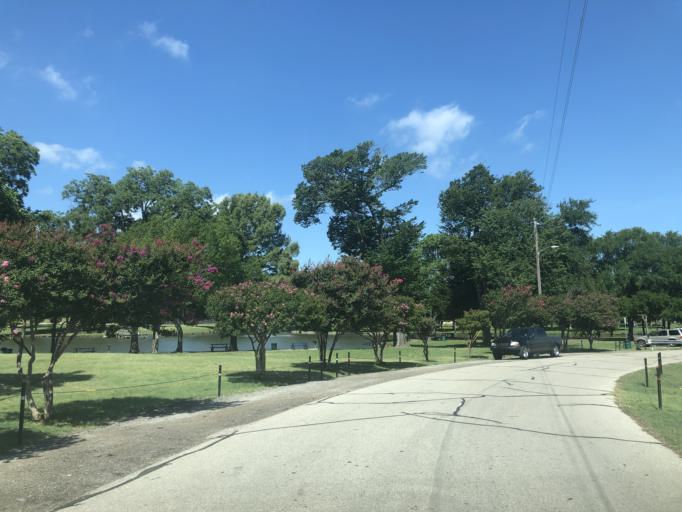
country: US
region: Texas
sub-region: Dallas County
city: Duncanville
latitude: 32.6558
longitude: -96.9194
